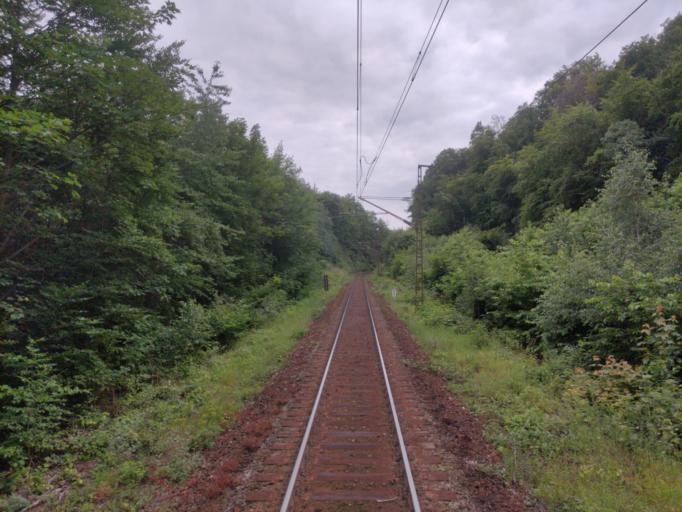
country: DE
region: Saxony-Anhalt
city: Blankenburg
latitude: 51.7935
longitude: 10.9265
